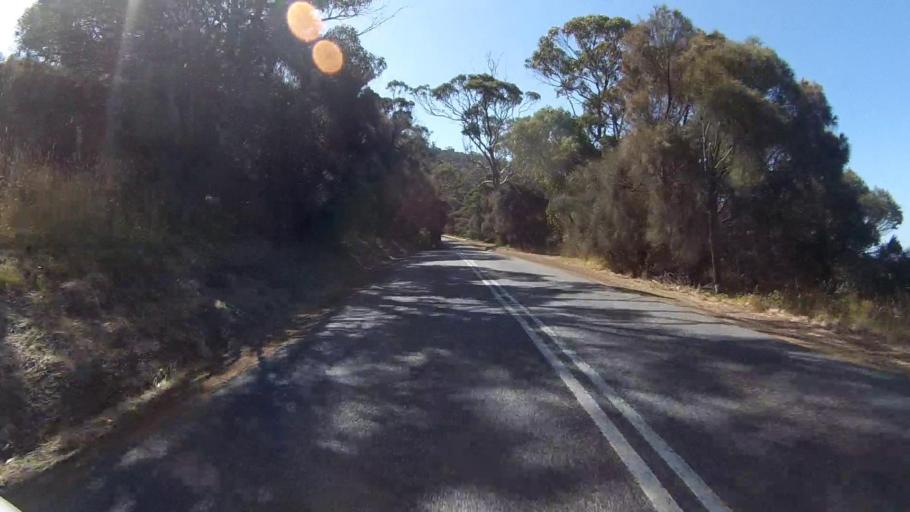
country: AU
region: Tasmania
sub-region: Sorell
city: Sorell
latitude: -42.2418
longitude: 148.0123
